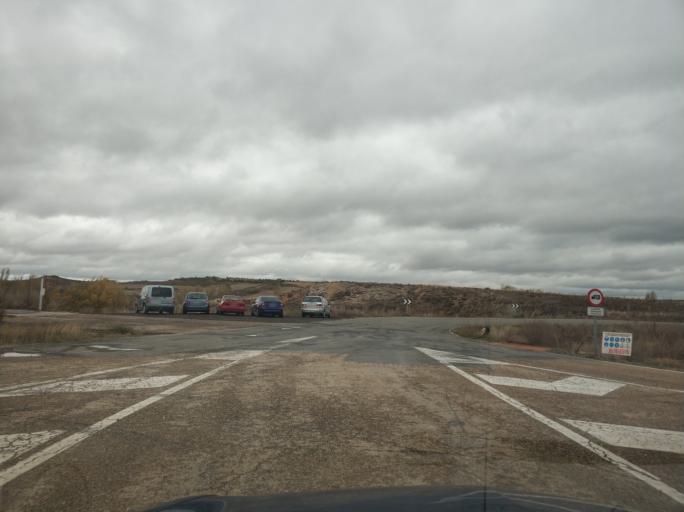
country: ES
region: Castille and Leon
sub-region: Provincia de Soria
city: San Esteban de Gormaz
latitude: 41.5807
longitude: -3.2055
